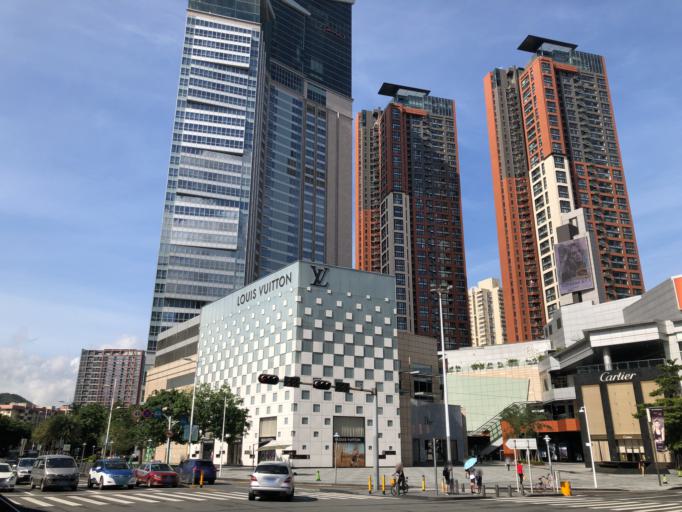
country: CN
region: Guangdong
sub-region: Shenzhen
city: Shenzhen
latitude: 22.5415
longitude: 114.1068
